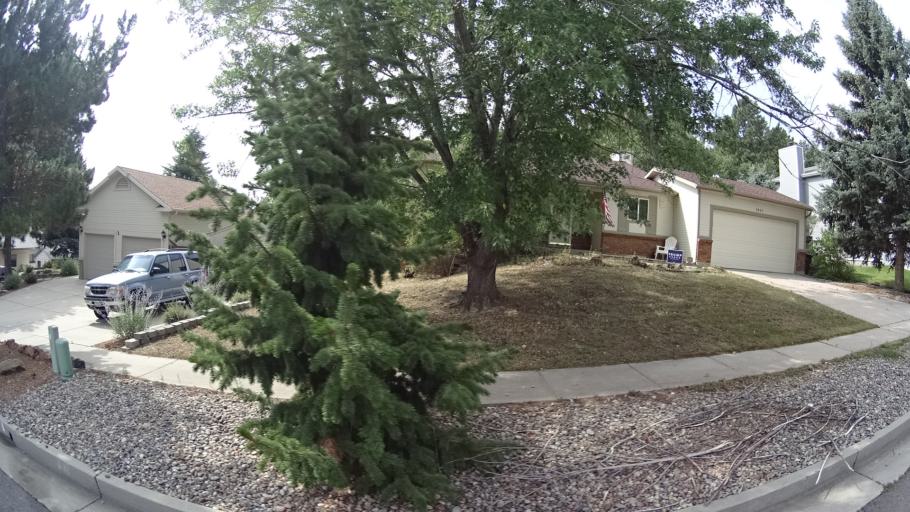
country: US
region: Colorado
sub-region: El Paso County
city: Colorado Springs
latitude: 38.8917
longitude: -104.7935
